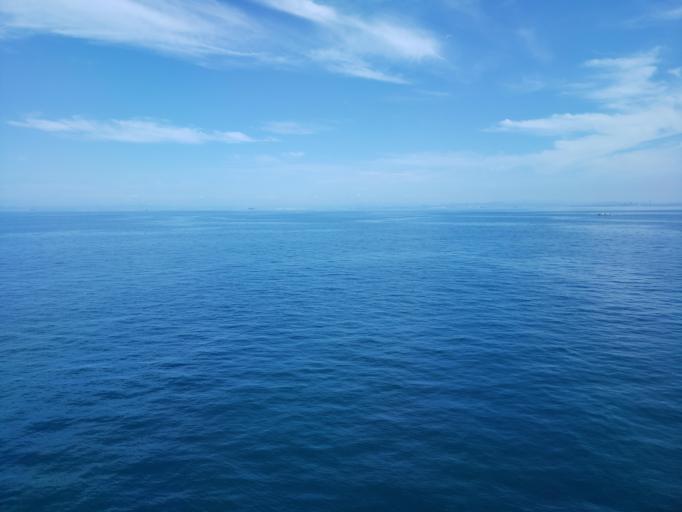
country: JP
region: Hyogo
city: Kakogawacho-honmachi
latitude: 34.5633
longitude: 134.7791
